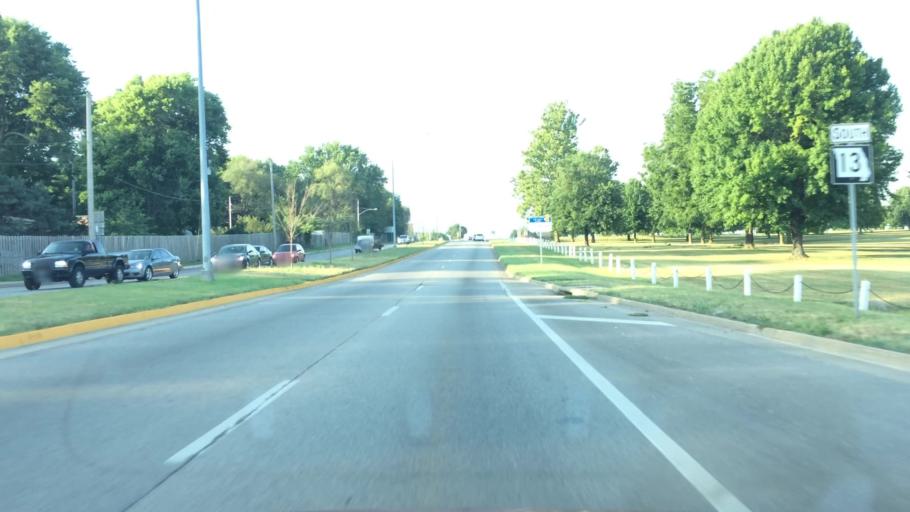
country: US
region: Missouri
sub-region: Greene County
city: Springfield
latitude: 37.1816
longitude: -93.3180
